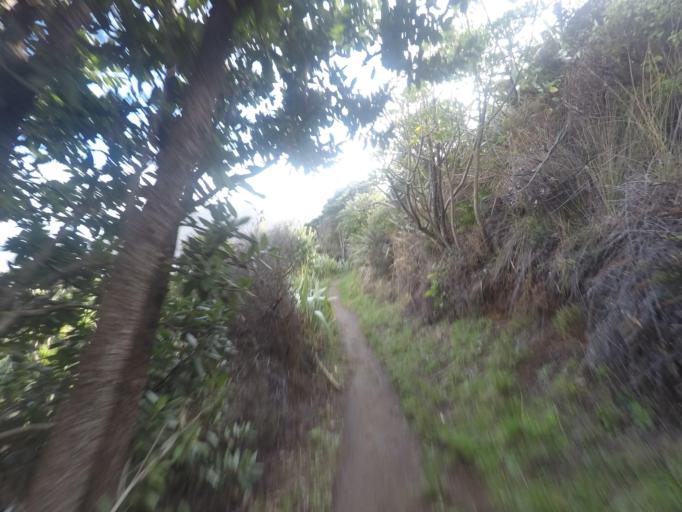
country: NZ
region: Auckland
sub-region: Auckland
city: Muriwai Beach
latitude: -36.8861
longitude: 174.4399
